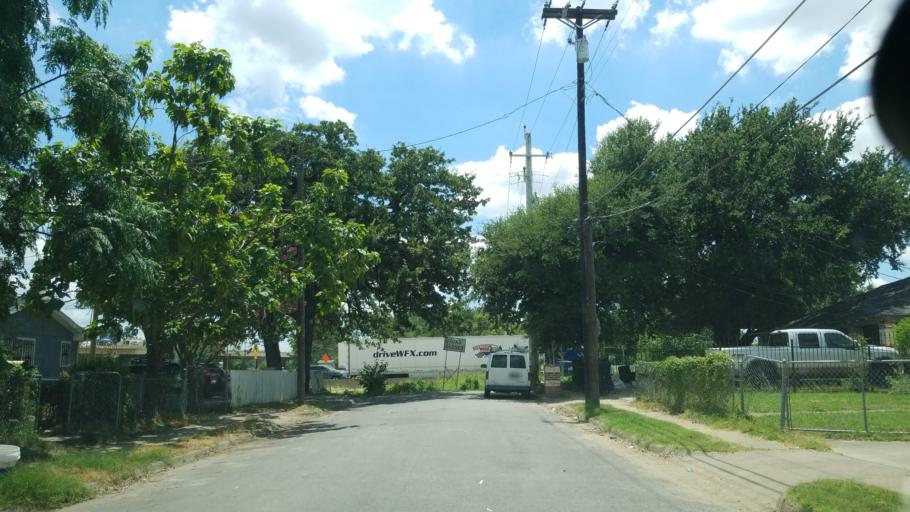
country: US
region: Texas
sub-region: Dallas County
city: Dallas
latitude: 32.7476
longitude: -96.7584
